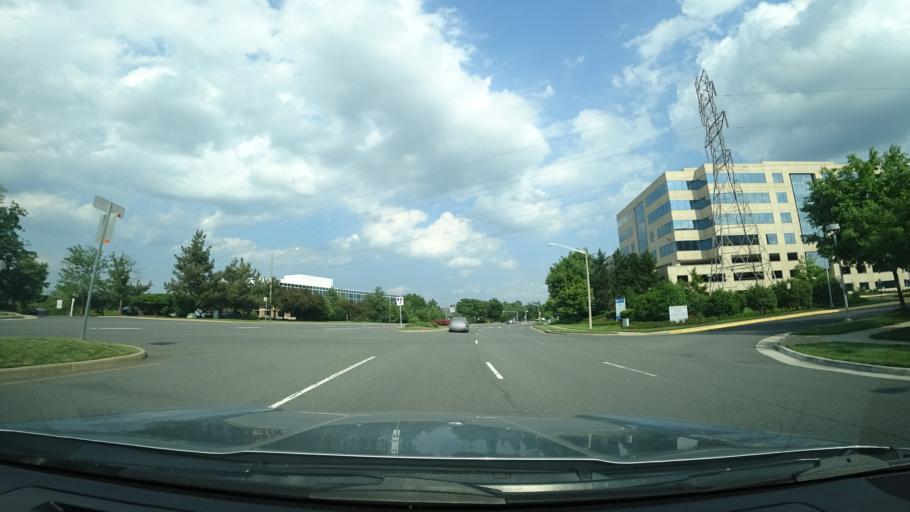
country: US
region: Virginia
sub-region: Fairfax County
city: Herndon
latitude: 38.9552
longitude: -77.3907
